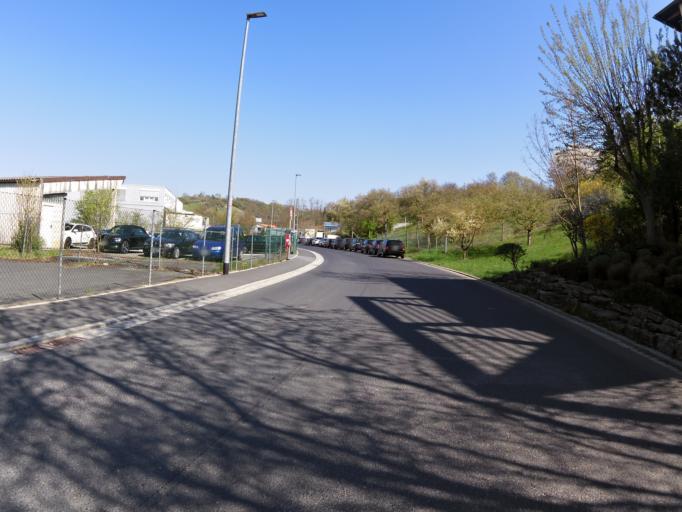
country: DE
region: Bavaria
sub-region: Regierungsbezirk Unterfranken
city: Rottendorf
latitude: 49.7907
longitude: 10.0369
